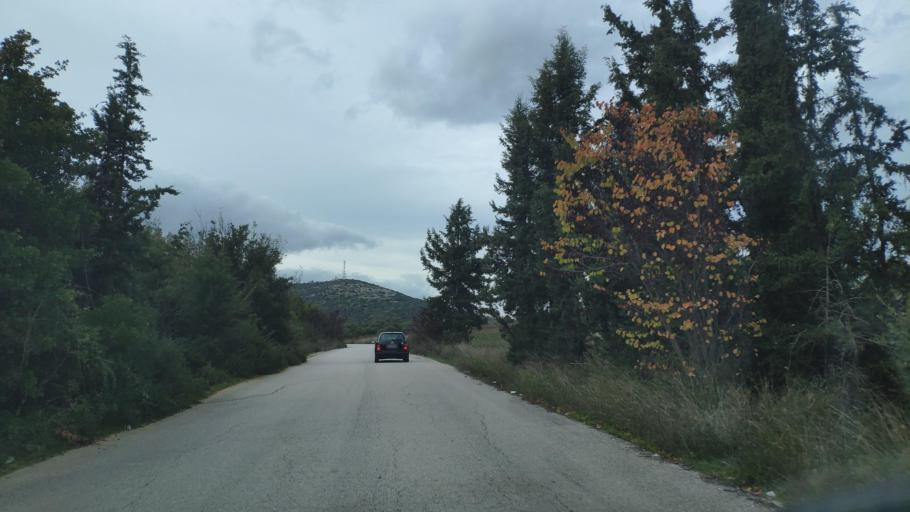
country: GR
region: Peloponnese
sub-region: Nomos Korinthias
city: Ayios Vasilios
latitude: 37.7931
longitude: 22.7312
